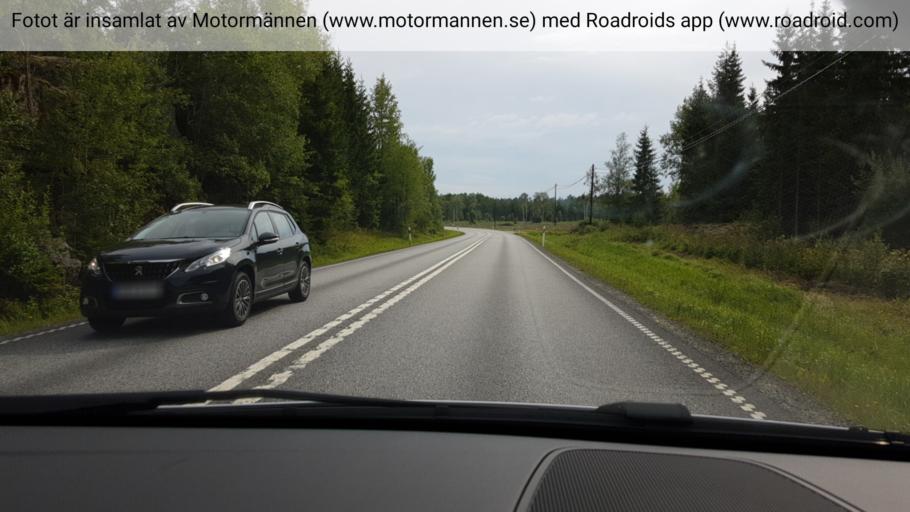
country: SE
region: Stockholm
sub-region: Norrtalje Kommun
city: Hallstavik
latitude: 60.0646
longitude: 18.5239
